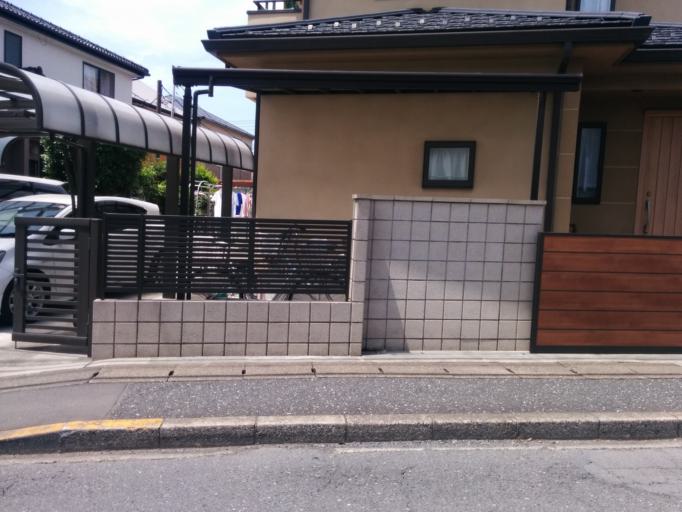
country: JP
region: Tokyo
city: Higashimurayama-shi
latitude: 35.7552
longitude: 139.4805
